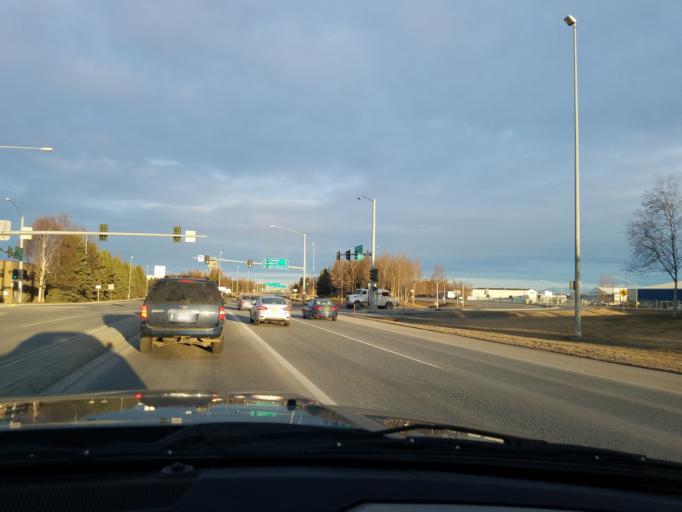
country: US
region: Alaska
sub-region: Anchorage Municipality
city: Anchorage
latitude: 61.1767
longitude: -149.9670
